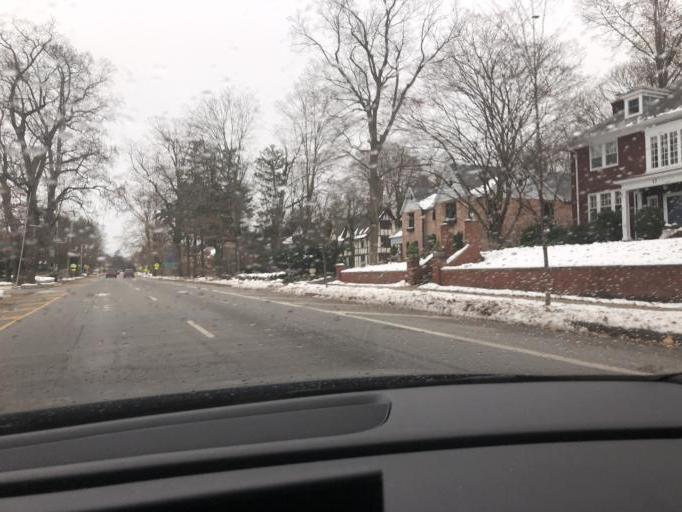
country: US
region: New Jersey
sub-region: Morris County
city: Morristown
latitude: 40.7961
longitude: -74.4650
